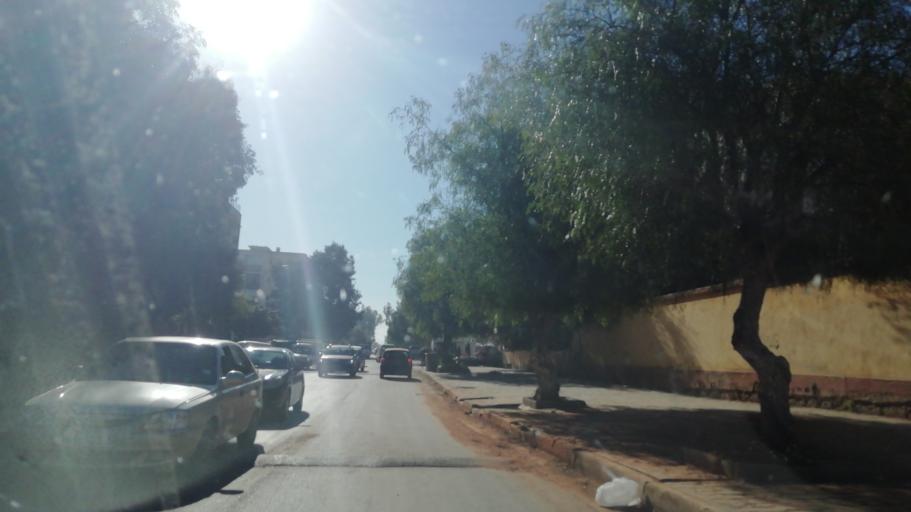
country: DZ
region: Oran
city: Oran
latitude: 35.6716
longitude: -0.6498
